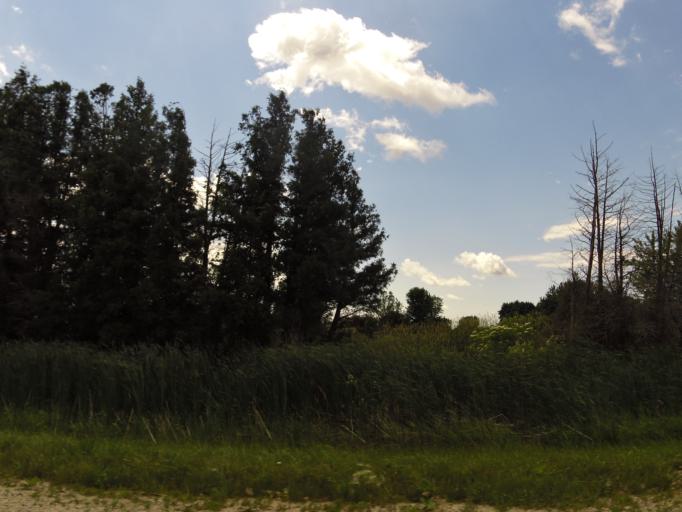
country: US
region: Iowa
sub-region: Fayette County
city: Oelwein
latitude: 42.7149
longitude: -91.9674
